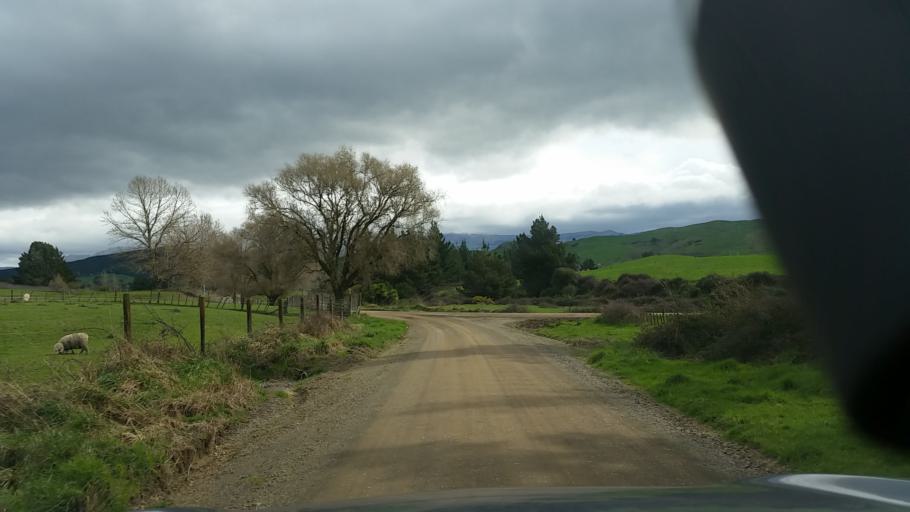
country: NZ
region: Hawke's Bay
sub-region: Napier City
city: Napier
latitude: -39.1886
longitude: 176.9119
